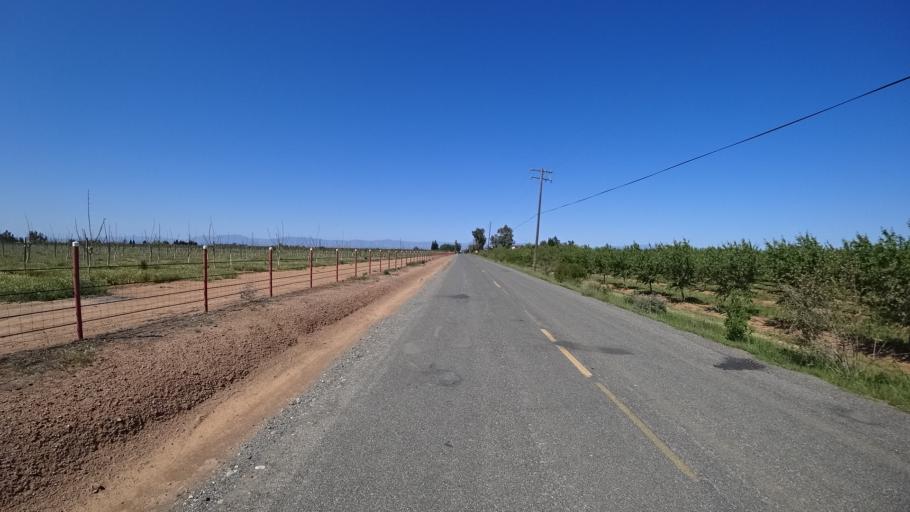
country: US
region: California
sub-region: Glenn County
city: Orland
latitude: 39.6966
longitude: -122.1740
